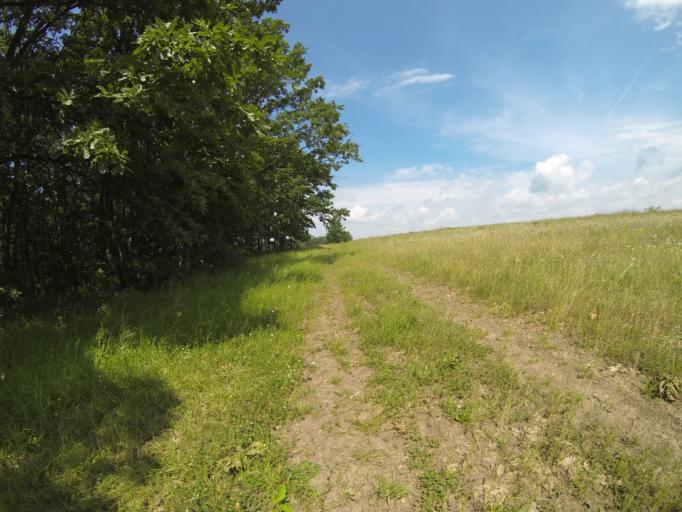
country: RO
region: Gorj
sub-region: Comuna Crusetu
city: Crusetu
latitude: 44.6268
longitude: 23.6152
